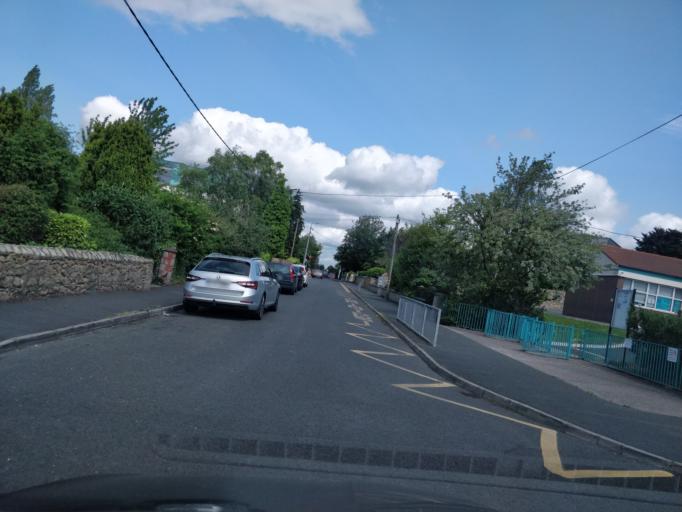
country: IE
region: Leinster
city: Balally
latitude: 53.2885
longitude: -6.2386
